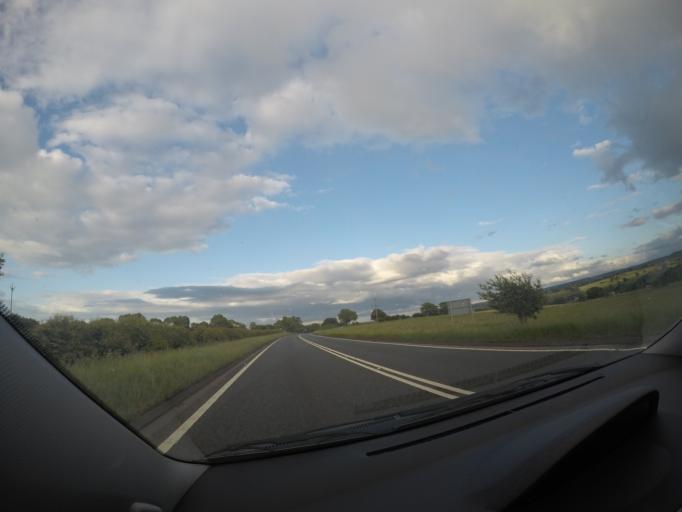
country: GB
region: England
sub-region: County Durham
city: Bowes
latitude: 54.5193
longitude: -2.0062
